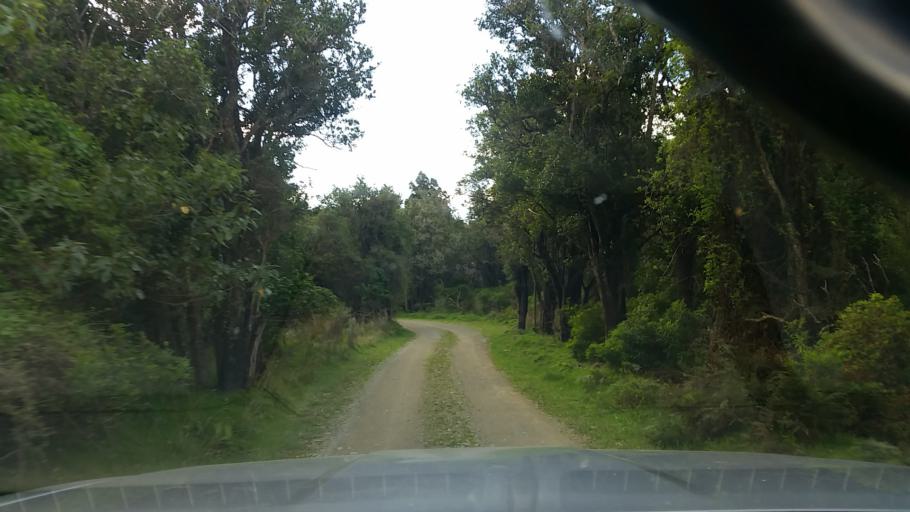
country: NZ
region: Marlborough
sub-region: Marlborough District
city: Picton
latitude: -41.0568
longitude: 174.1107
